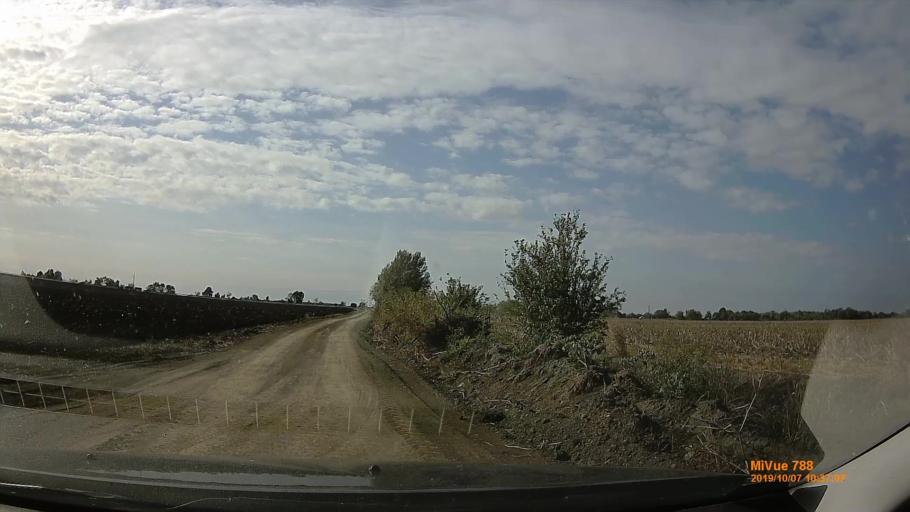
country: HU
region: Bekes
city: Kondoros
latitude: 46.7512
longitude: 20.8501
